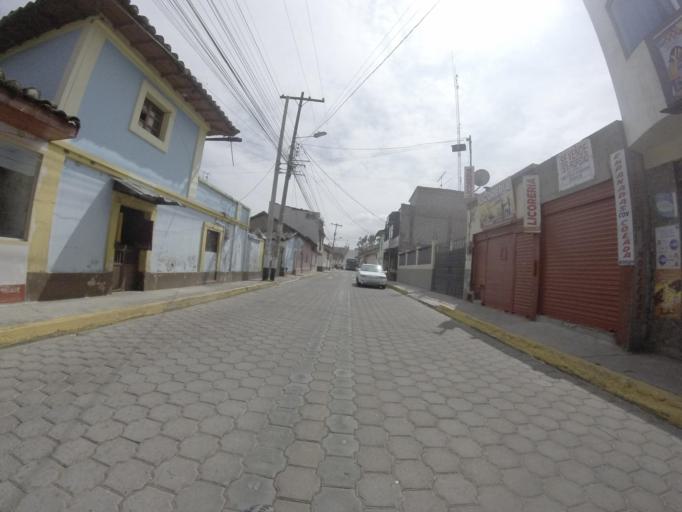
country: EC
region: Pichincha
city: Cayambe
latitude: 0.1382
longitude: -78.0819
